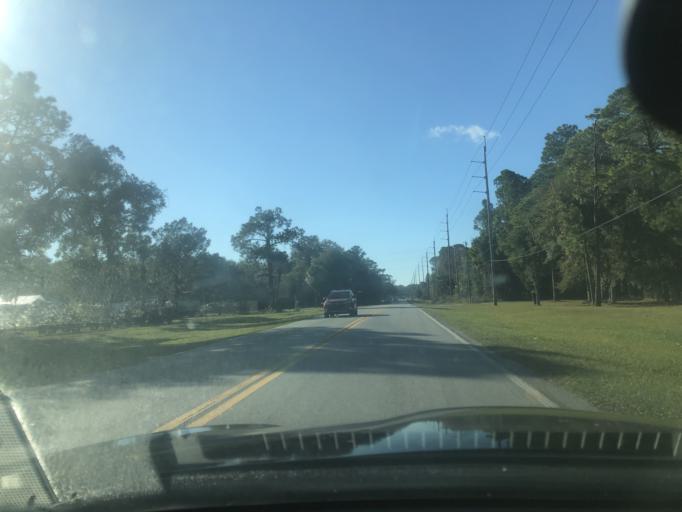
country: US
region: Florida
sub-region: Citrus County
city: Homosassa Springs
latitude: 28.8038
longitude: -82.5698
